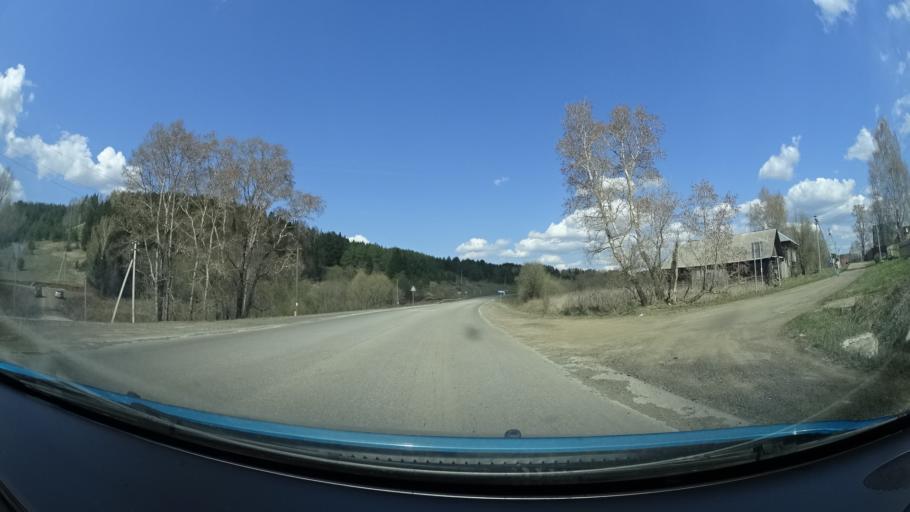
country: RU
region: Perm
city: Osa
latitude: 57.2234
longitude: 55.5878
